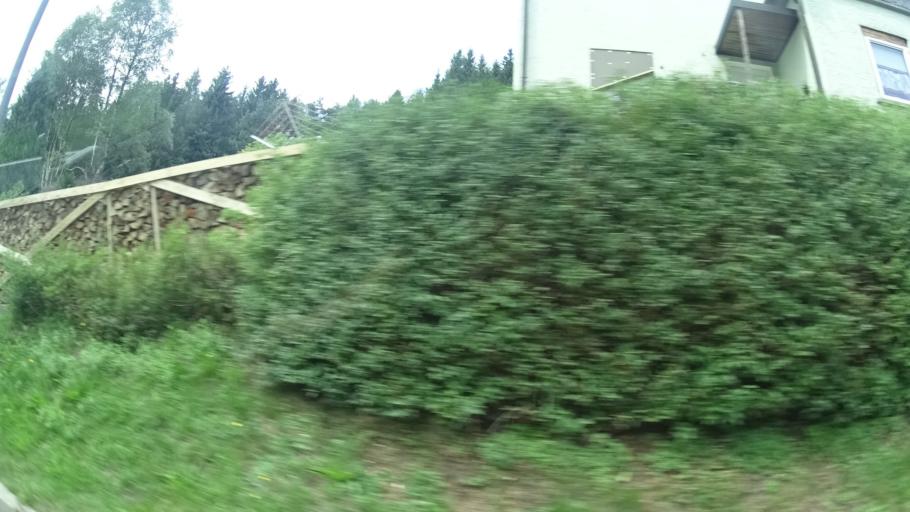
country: DE
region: Bavaria
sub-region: Upper Franconia
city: Tettau
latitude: 50.4740
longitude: 11.2600
